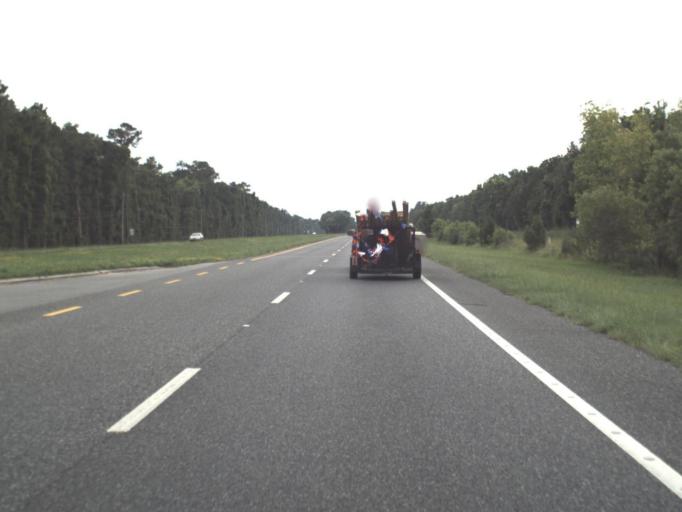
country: US
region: Florida
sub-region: Levy County
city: Williston Highlands
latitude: 29.2422
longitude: -82.7163
